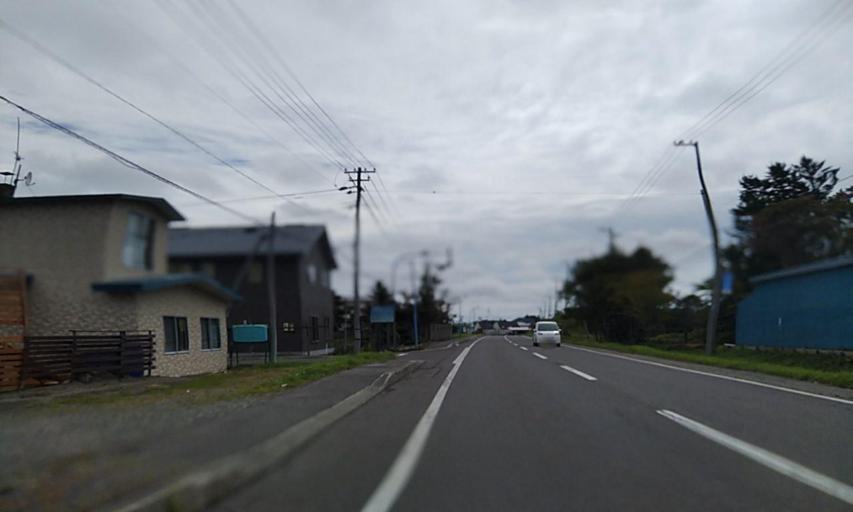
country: JP
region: Hokkaido
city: Shibetsu
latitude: 43.5793
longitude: 145.2119
